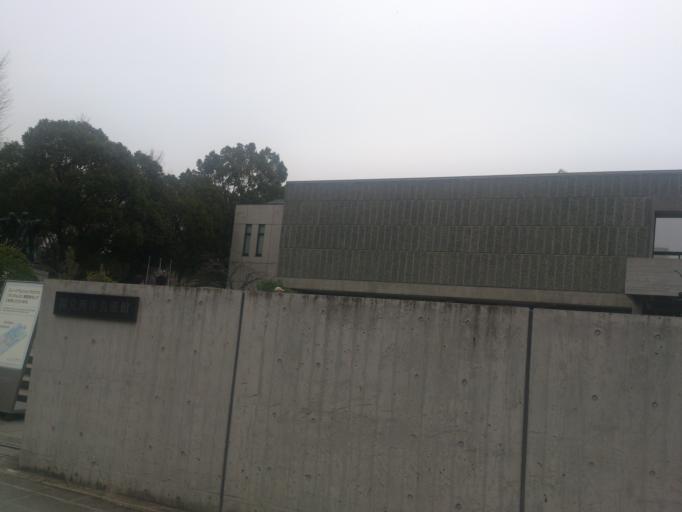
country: JP
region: Tokyo
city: Tokyo
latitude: 35.7148
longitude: 139.7756
